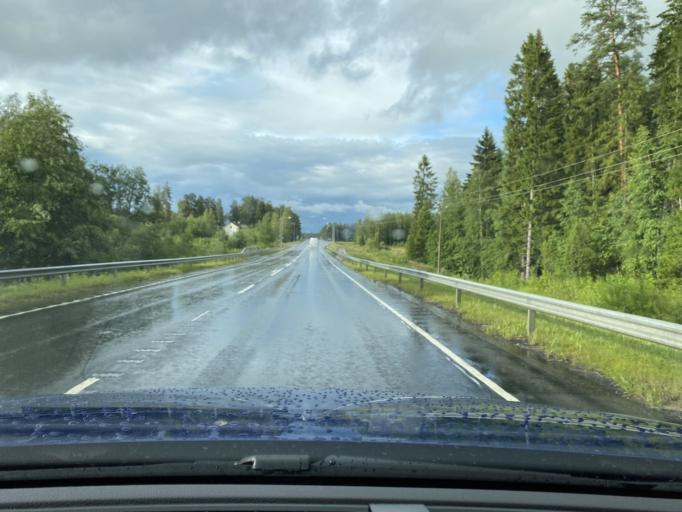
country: FI
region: Uusimaa
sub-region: Helsinki
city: Nurmijaervi
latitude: 60.4688
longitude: 24.8386
